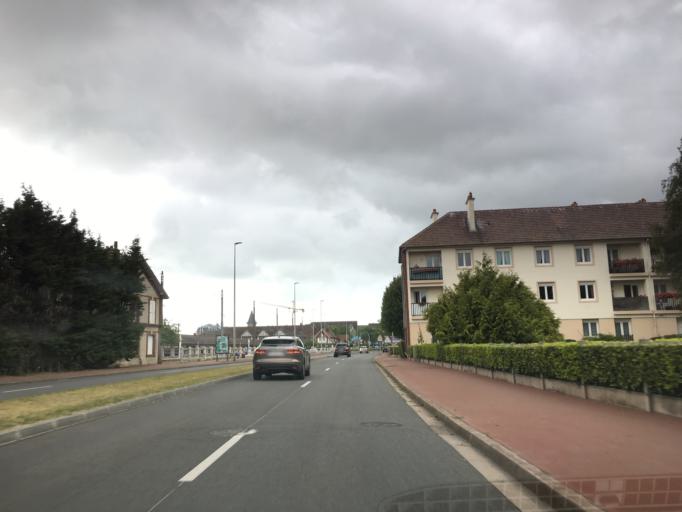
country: FR
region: Lower Normandy
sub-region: Departement du Calvados
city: Trouville-sur-Mer
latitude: 49.3575
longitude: 0.0869
